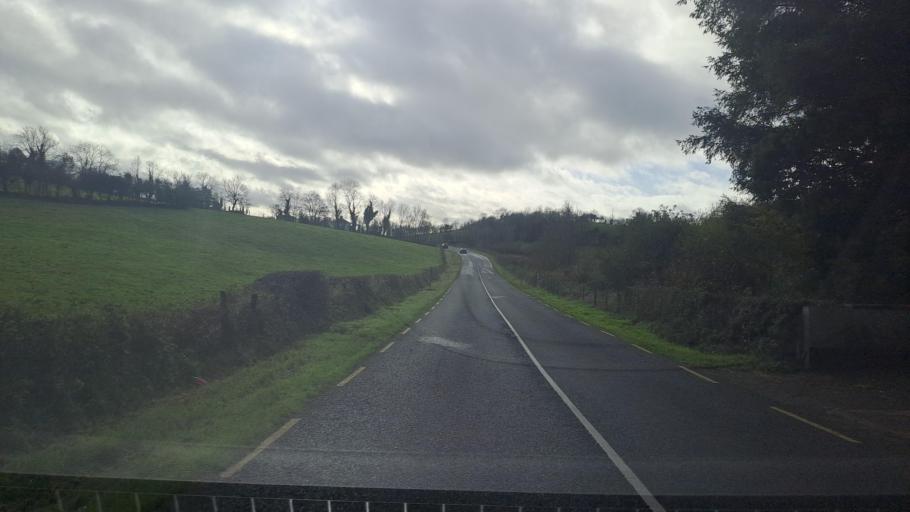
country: IE
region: Ulster
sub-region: County Monaghan
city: Monaghan
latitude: 54.1761
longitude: -6.9964
